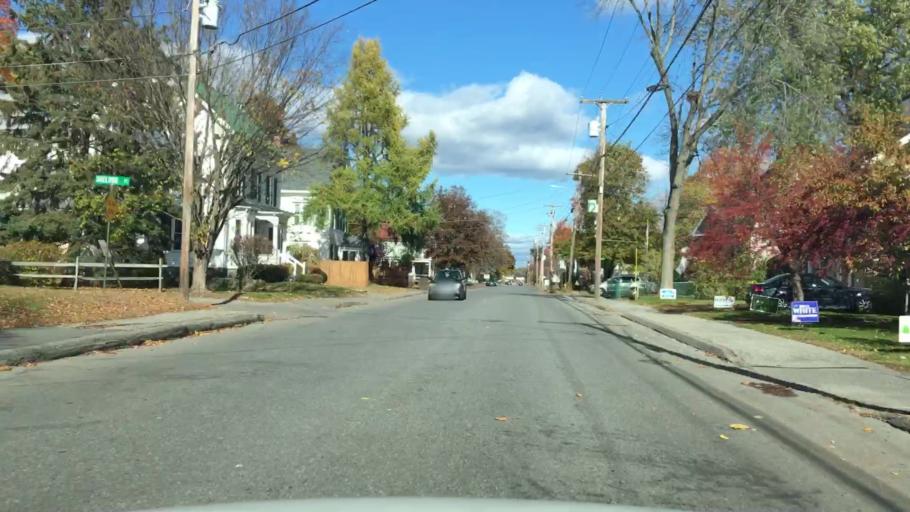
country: US
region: Maine
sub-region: Kennebec County
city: Waterville
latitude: 44.5512
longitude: -69.6355
